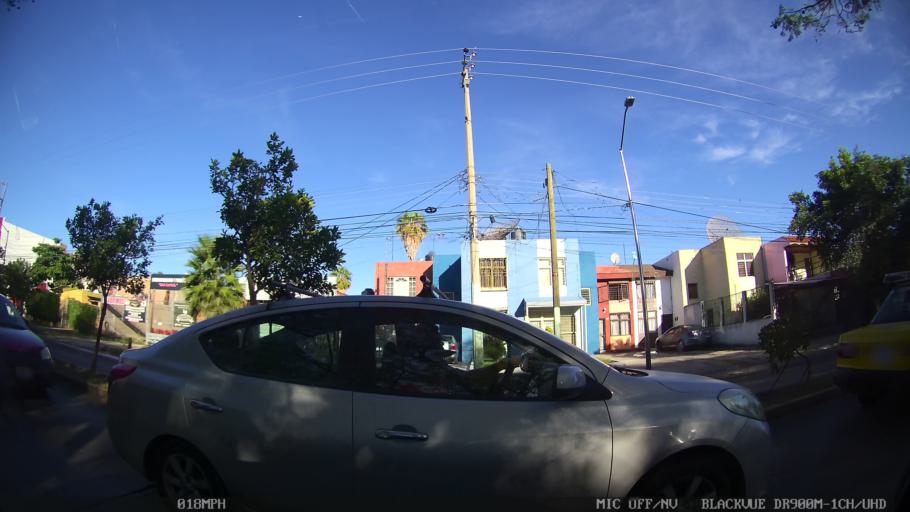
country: MX
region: Jalisco
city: Tlaquepaque
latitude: 20.6538
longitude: -103.3000
